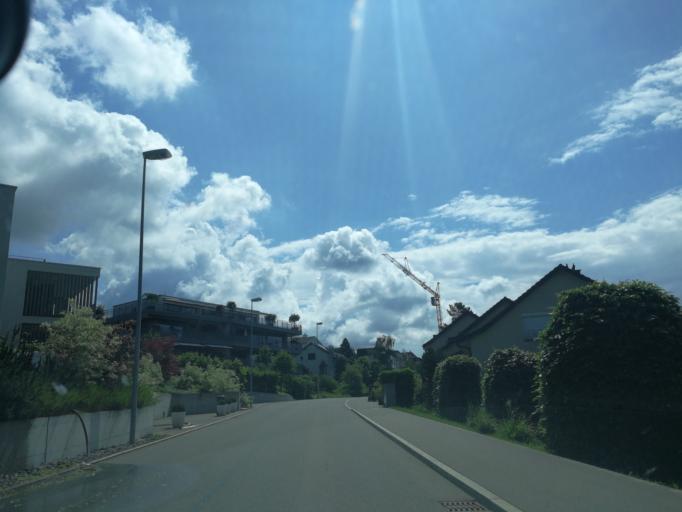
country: CH
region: Zurich
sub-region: Bezirk Meilen
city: Erlenbach / rechts des Dorfbachs oberhalb Bahnlinie
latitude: 47.3085
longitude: 8.5977
